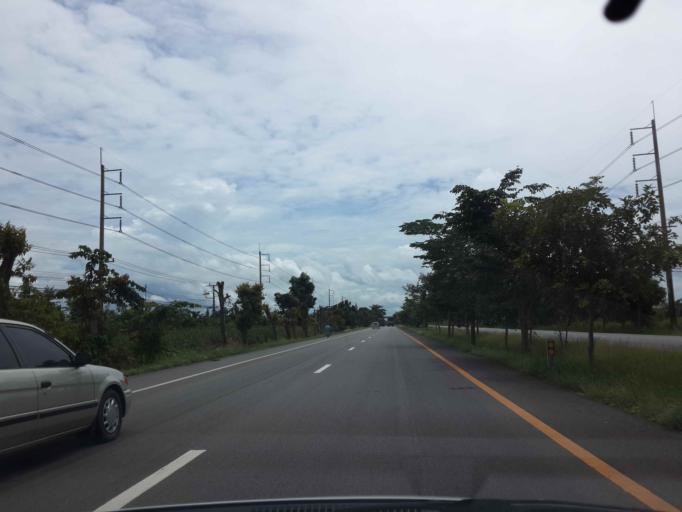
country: TH
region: Ratchaburi
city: Pak Tho
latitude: 13.4170
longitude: 99.8100
